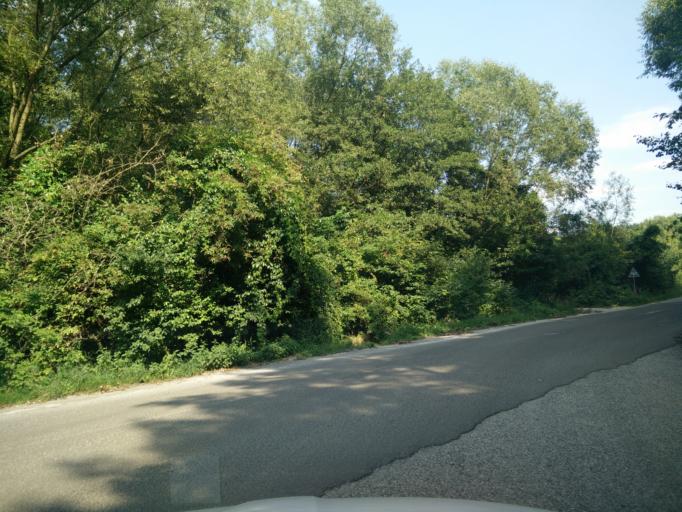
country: SK
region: Nitriansky
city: Prievidza
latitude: 48.7351
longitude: 18.6400
